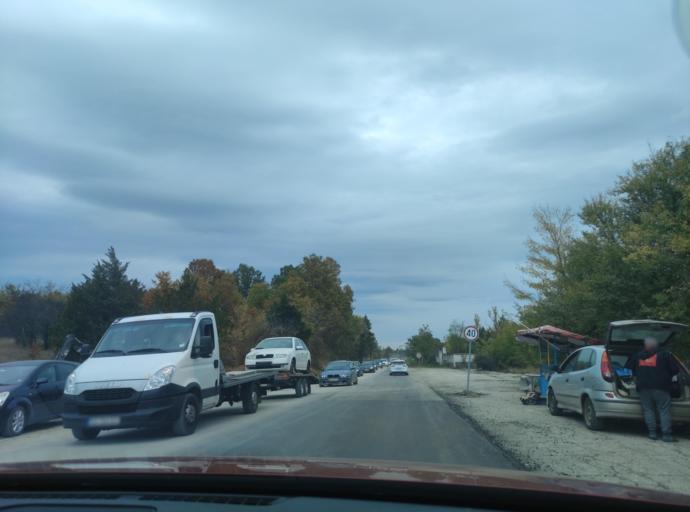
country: BG
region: Montana
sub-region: Obshtina Montana
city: Montana
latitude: 43.3814
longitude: 23.2423
